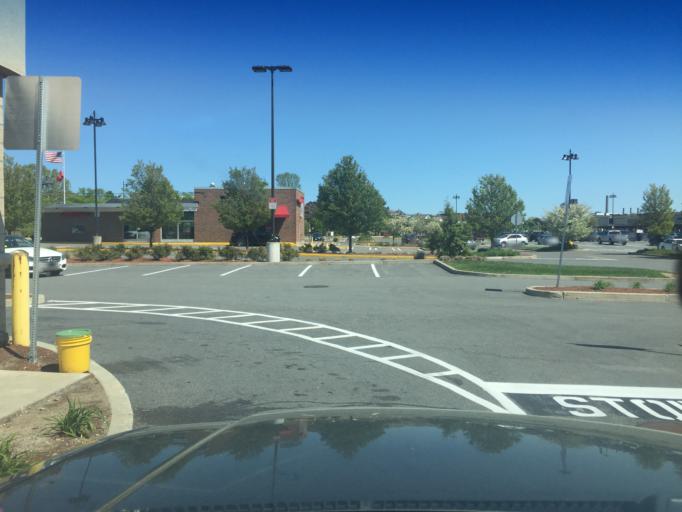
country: US
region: Massachusetts
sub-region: Middlesex County
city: Medford
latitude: 42.4098
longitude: -71.0863
